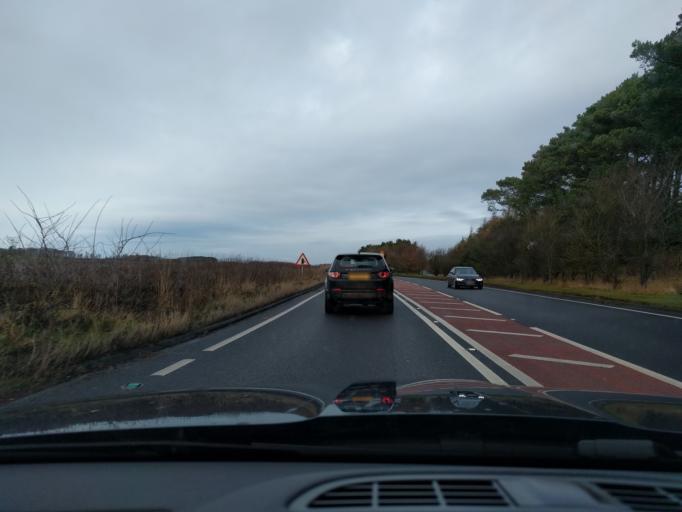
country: GB
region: England
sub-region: Northumberland
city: Ancroft
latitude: 55.7289
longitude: -1.9867
